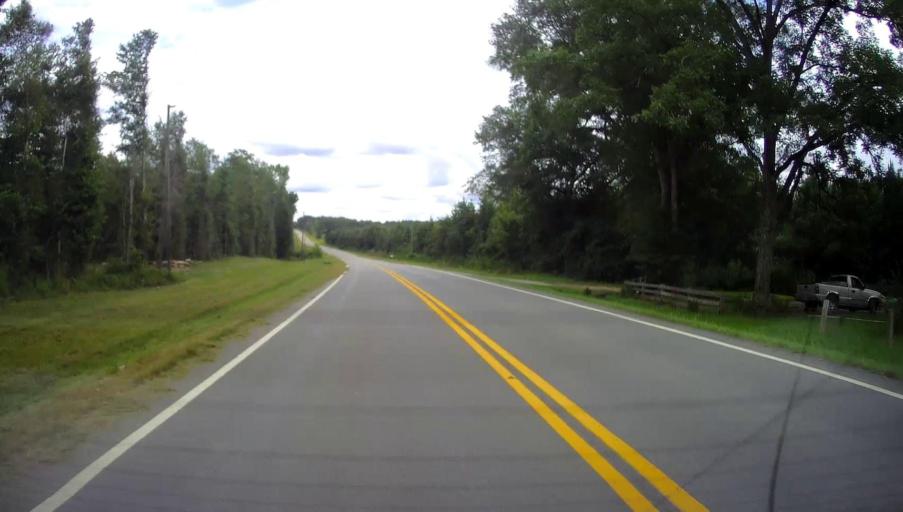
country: US
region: Georgia
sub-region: Schley County
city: Ellaville
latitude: 32.2628
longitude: -84.1998
